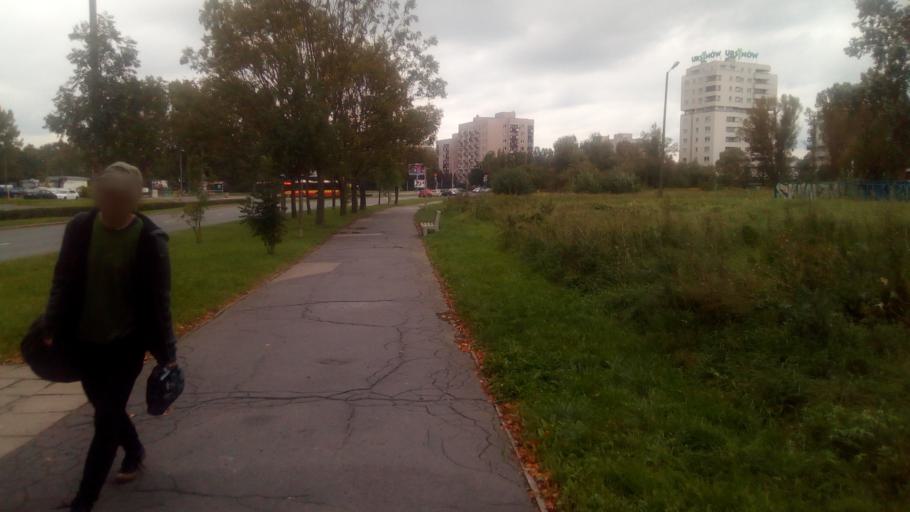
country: PL
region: Masovian Voivodeship
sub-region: Warszawa
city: Ursynow
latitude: 52.1532
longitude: 21.0494
